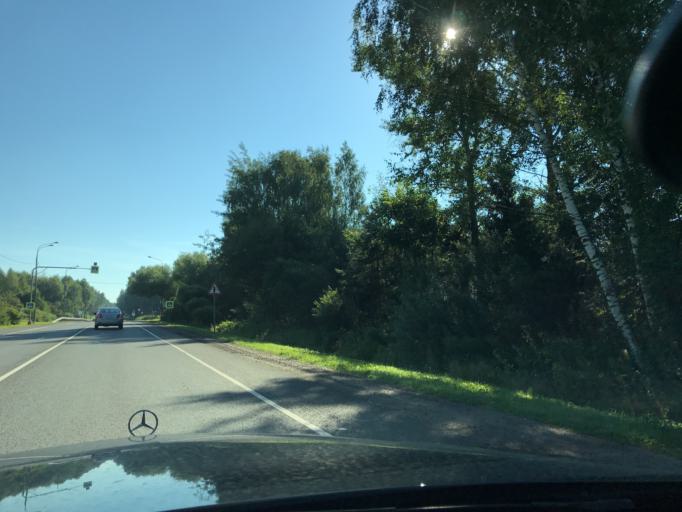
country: RU
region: Moskovskaya
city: Losino-Petrovskiy
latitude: 55.9599
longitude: 38.2580
